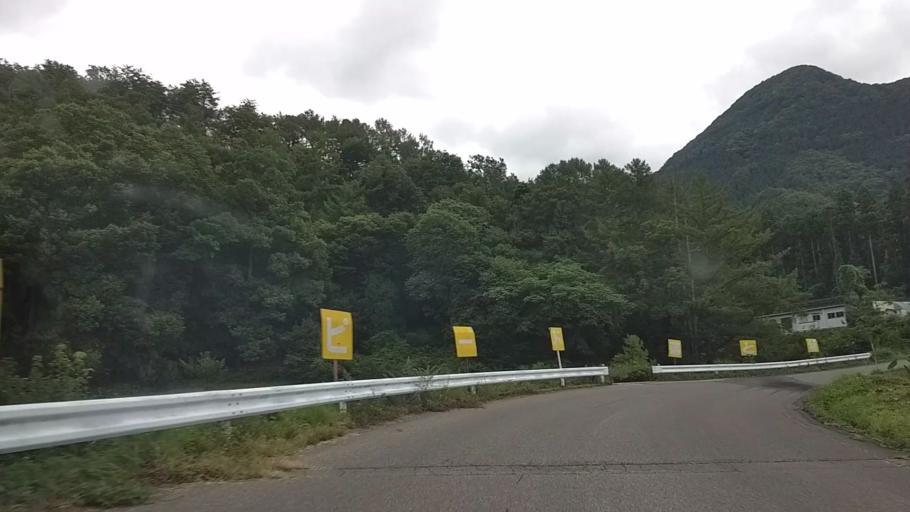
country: JP
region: Nagano
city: Iiyama
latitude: 36.8177
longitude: 138.3674
